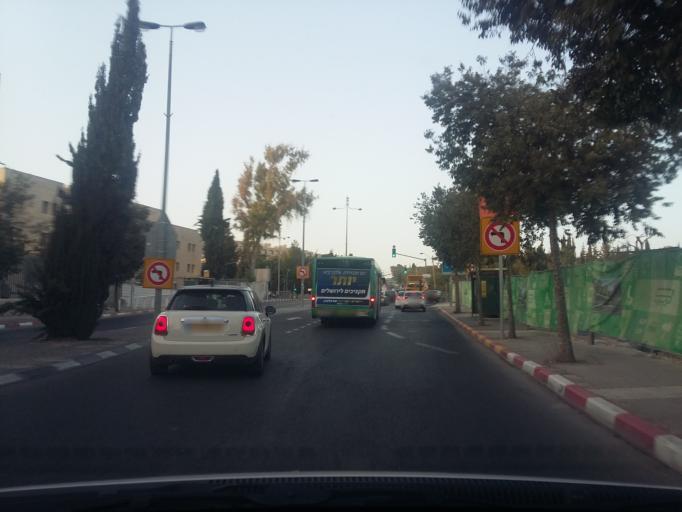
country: PS
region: West Bank
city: East Jerusalem
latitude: 31.7955
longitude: 35.2348
